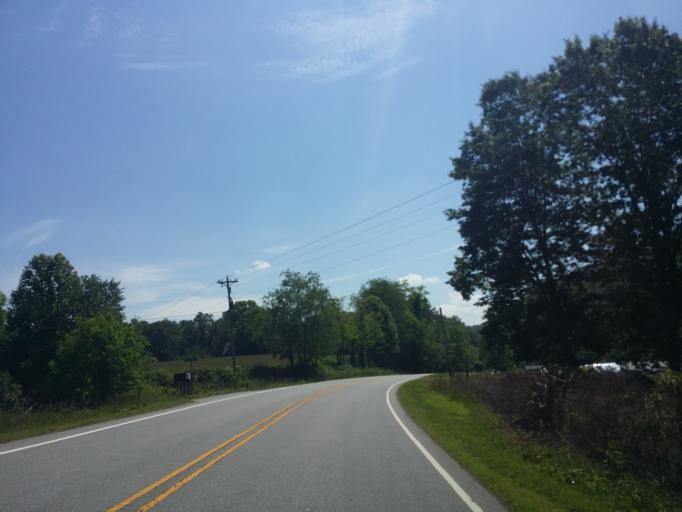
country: US
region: North Carolina
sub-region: Madison County
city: Marshall
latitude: 35.7039
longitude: -82.7981
